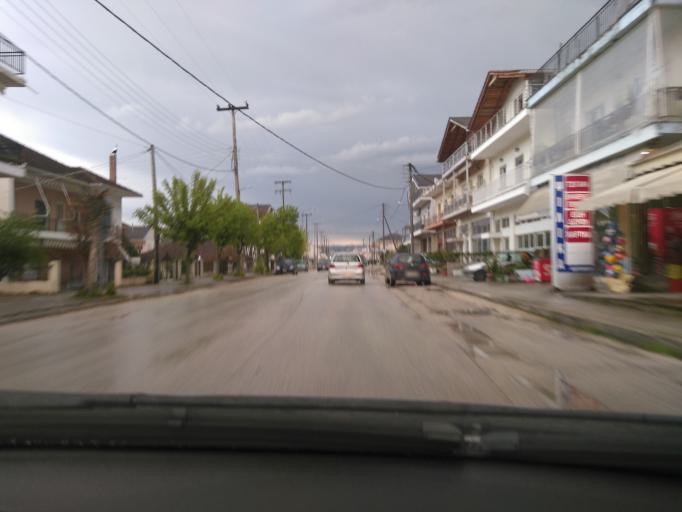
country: GR
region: Epirus
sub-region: Nomos Ioanninon
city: Anatoli
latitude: 39.6386
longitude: 20.8692
